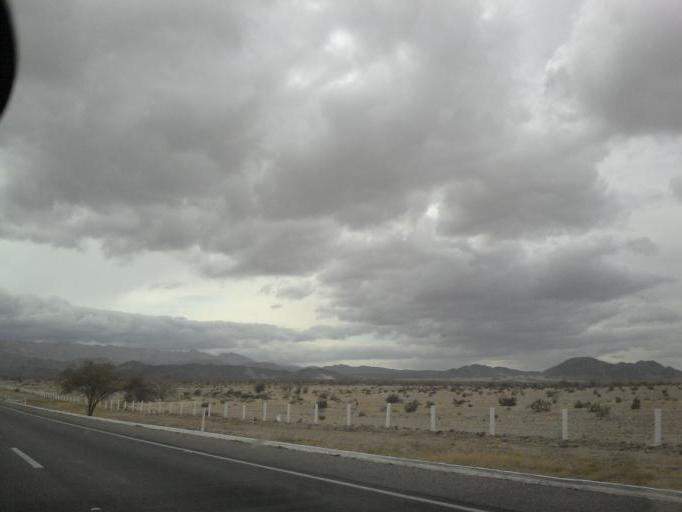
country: MX
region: Baja California
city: Progreso
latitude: 32.5647
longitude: -115.8786
